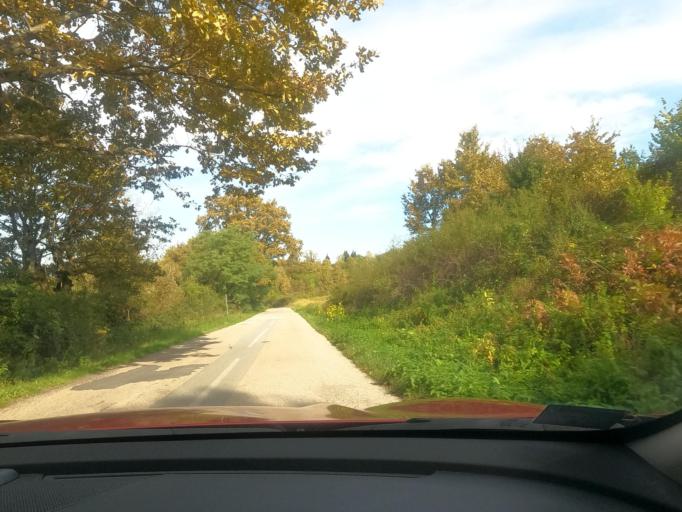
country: HR
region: Sisacko-Moslavacka
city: Glina
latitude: 45.2969
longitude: 16.1429
